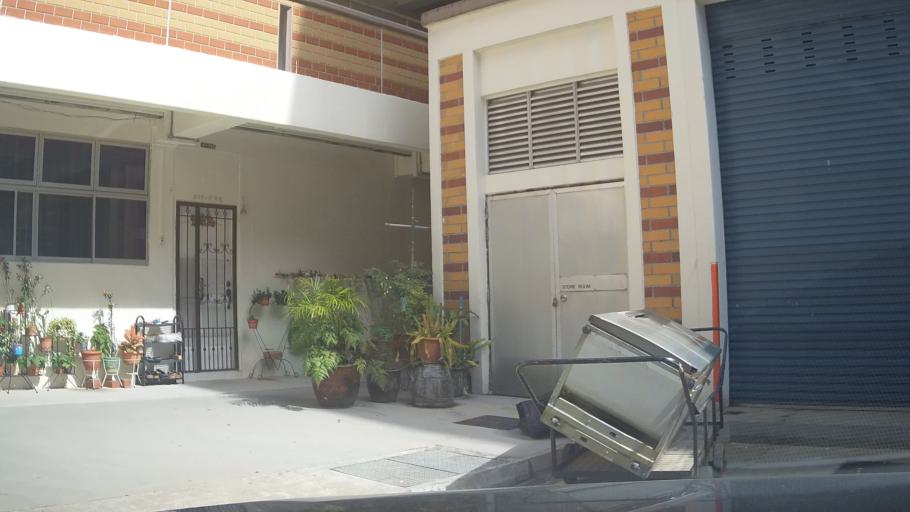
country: SG
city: Singapore
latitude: 1.3648
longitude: 103.9577
